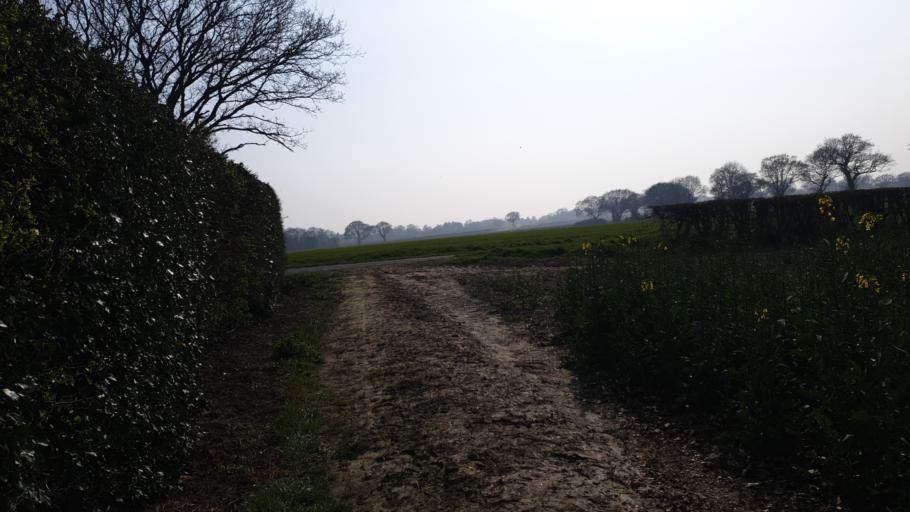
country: GB
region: England
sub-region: Essex
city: Mistley
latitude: 51.8923
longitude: 1.1194
